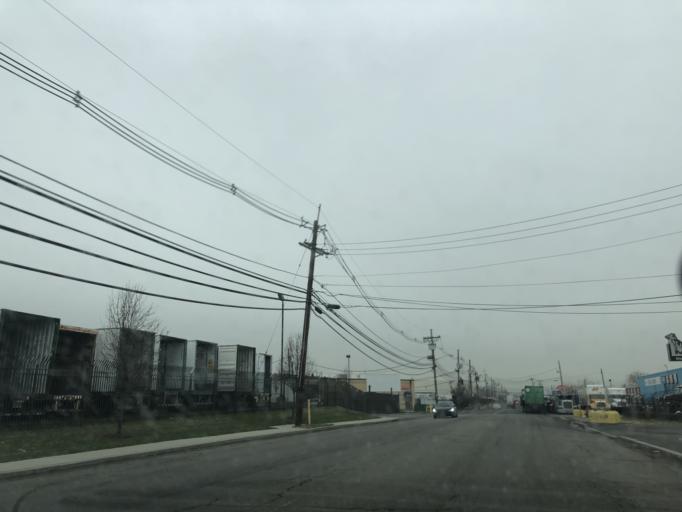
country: US
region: New Jersey
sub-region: Union County
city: Elizabeth
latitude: 40.6659
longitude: -74.1872
